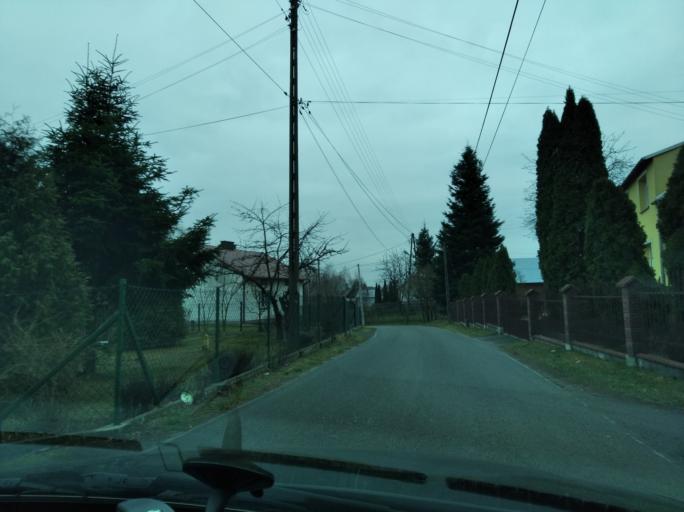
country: PL
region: Subcarpathian Voivodeship
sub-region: Powiat lancucki
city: Rakszawa
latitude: 50.1532
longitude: 22.2332
